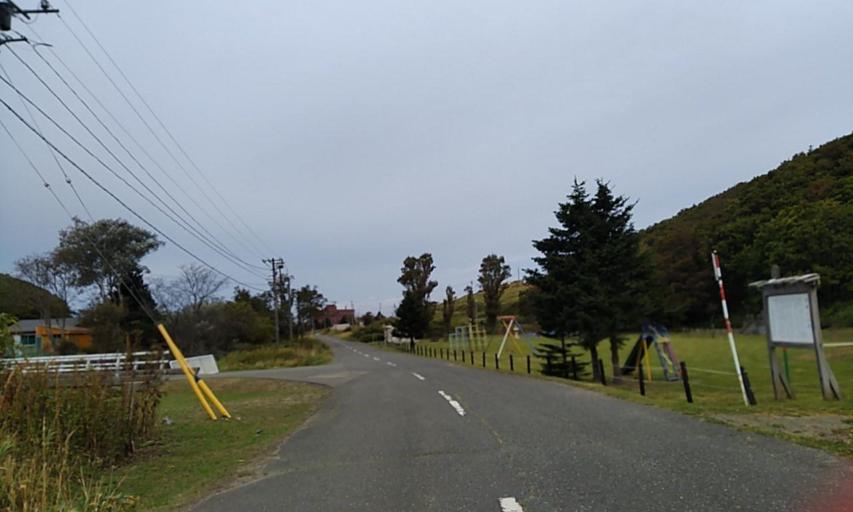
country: JP
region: Hokkaido
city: Makubetsu
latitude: 45.4853
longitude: 141.8846
